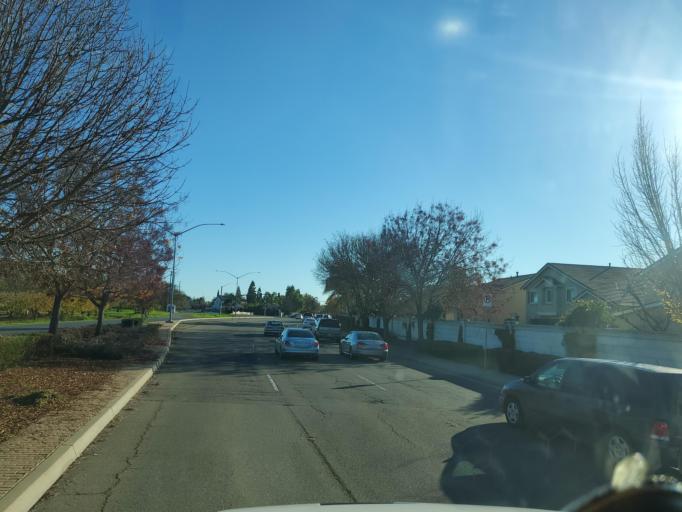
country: US
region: California
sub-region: San Joaquin County
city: August
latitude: 38.0074
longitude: -121.2722
